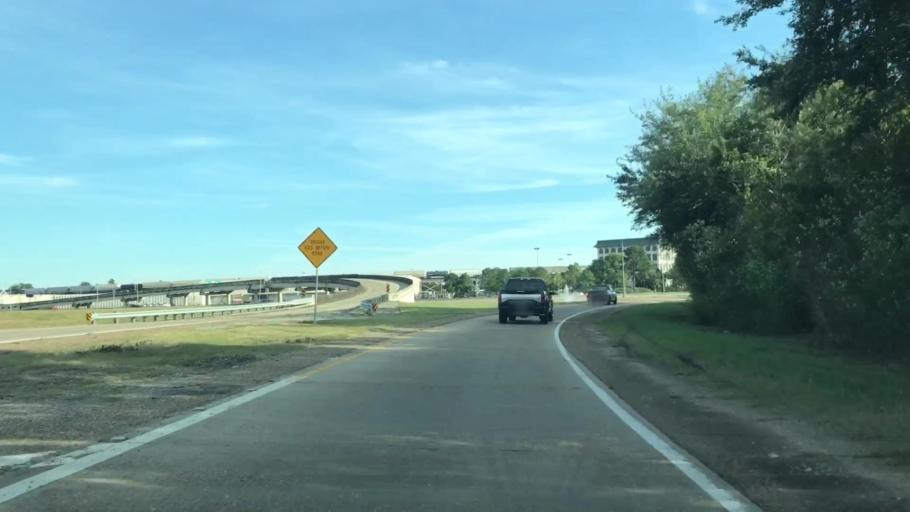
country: US
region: Louisiana
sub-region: Jefferson Parish
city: Elmwood
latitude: 29.9679
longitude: -90.1871
